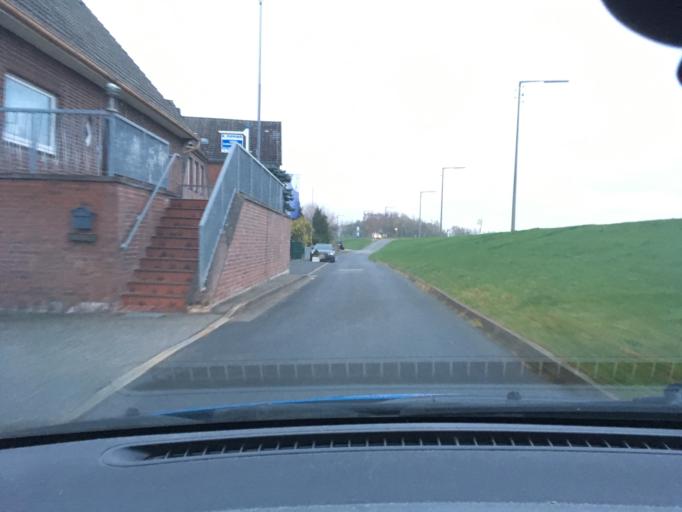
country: DE
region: Lower Saxony
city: Winsen
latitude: 53.3995
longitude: 10.2141
